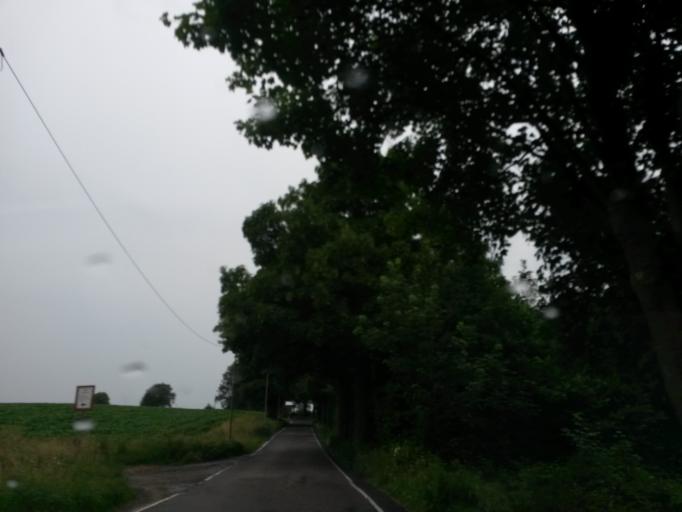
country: DE
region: North Rhine-Westphalia
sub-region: Regierungsbezirk Koln
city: Much
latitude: 50.9361
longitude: 7.3661
